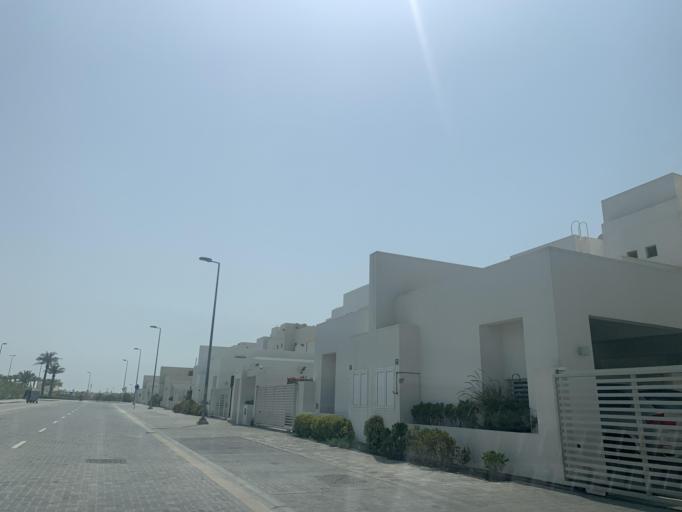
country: BH
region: Muharraq
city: Al Hadd
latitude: 26.2732
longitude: 50.6701
